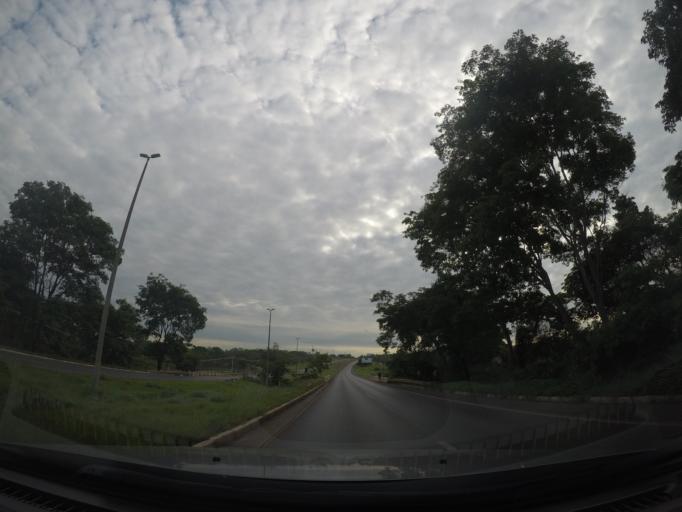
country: BR
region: Goias
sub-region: Planaltina
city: Planaltina
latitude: -15.5957
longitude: -47.6696
